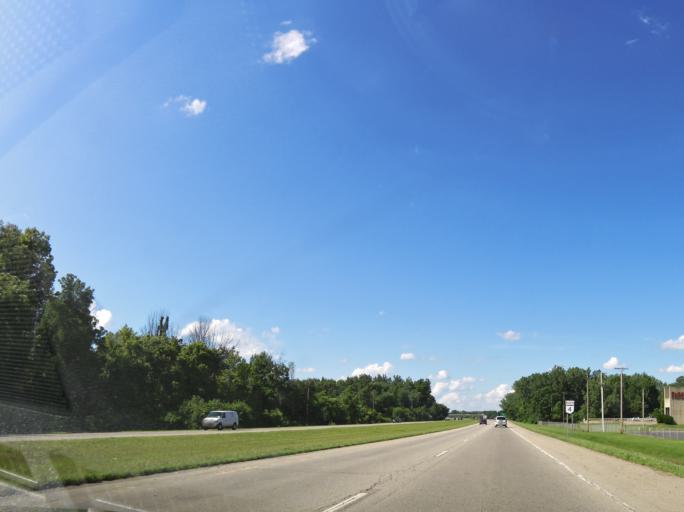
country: US
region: Ohio
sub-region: Greene County
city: Wright-Patterson AFB
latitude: 39.8370
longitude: -84.0605
